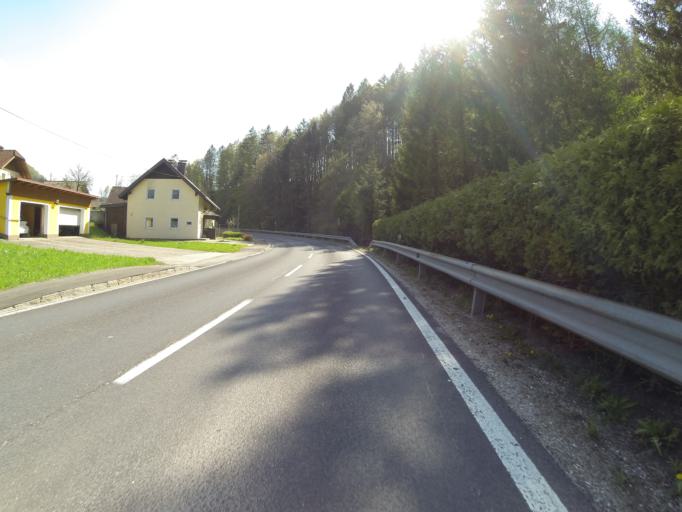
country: AT
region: Upper Austria
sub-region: Politischer Bezirk Gmunden
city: Altmunster
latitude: 47.9058
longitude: 13.7093
